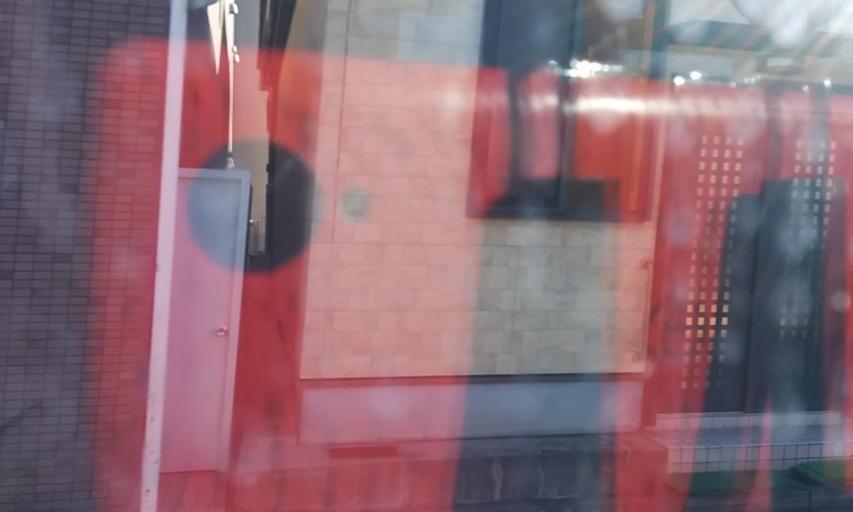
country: JP
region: Wakayama
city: Wakayama-shi
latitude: 34.2370
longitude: 135.1745
